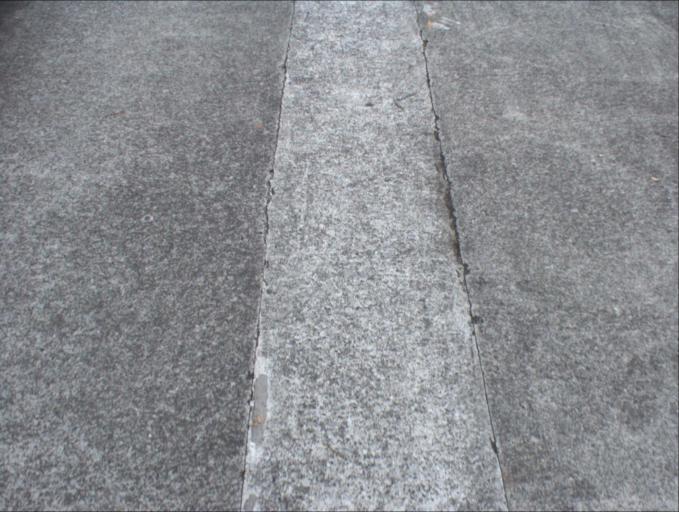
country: AU
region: Queensland
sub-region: Logan
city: Springwood
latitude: -27.6184
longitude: 153.1262
